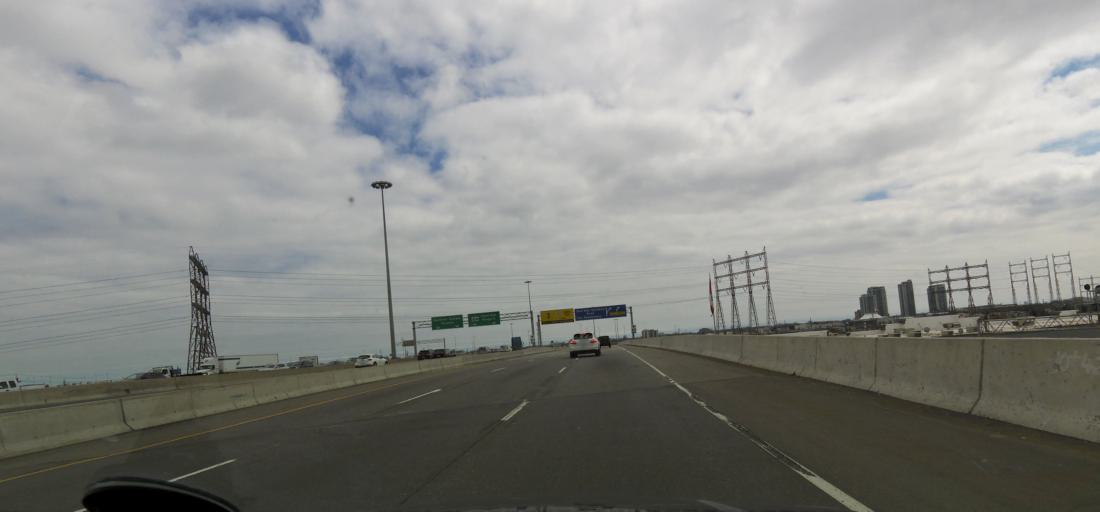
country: CA
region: Ontario
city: Etobicoke
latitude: 43.6230
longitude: -79.5550
